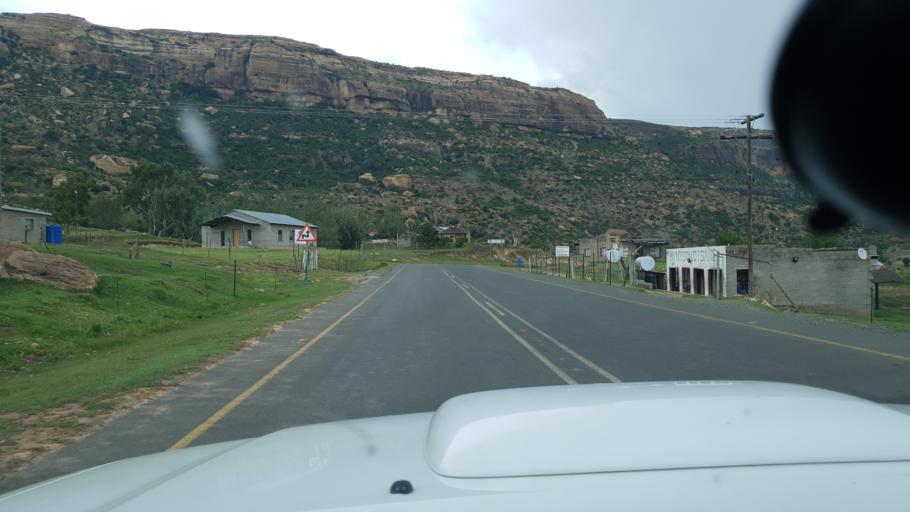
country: LS
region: Maseru
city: Maseru
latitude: -29.4651
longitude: 27.4998
